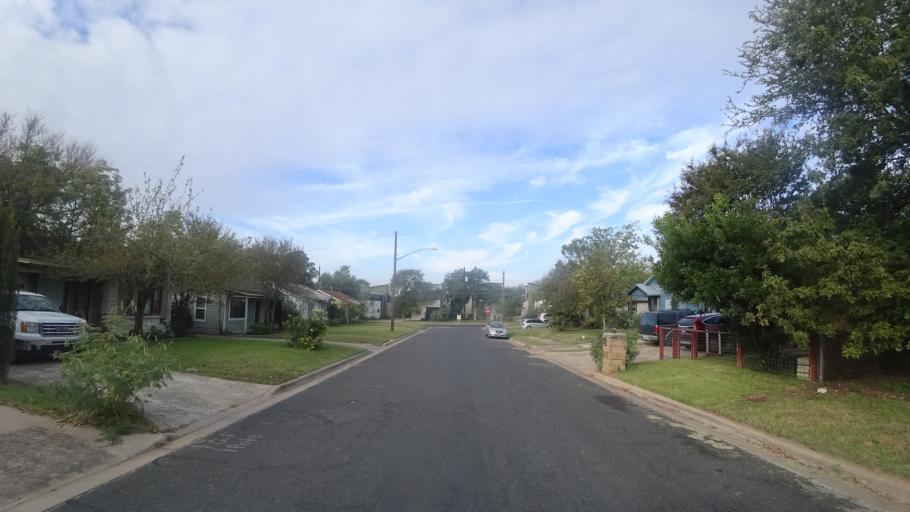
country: US
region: Texas
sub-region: Travis County
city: Austin
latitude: 30.2809
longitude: -97.7046
